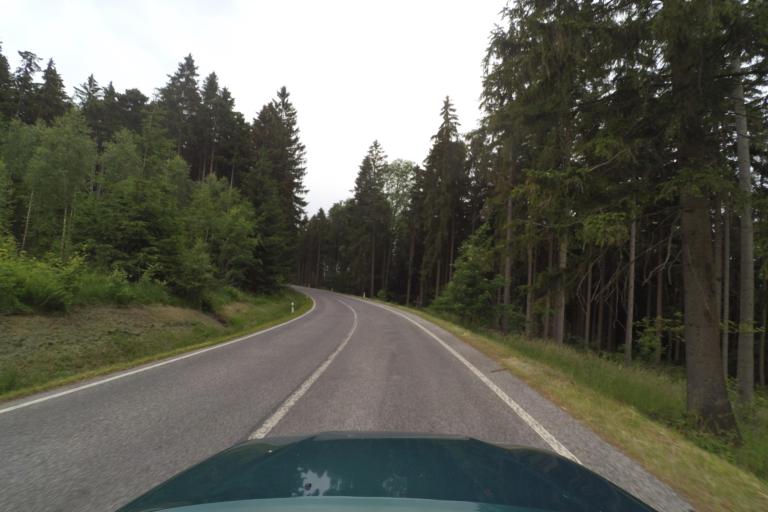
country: CZ
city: Osecna
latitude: 50.7301
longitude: 14.9602
